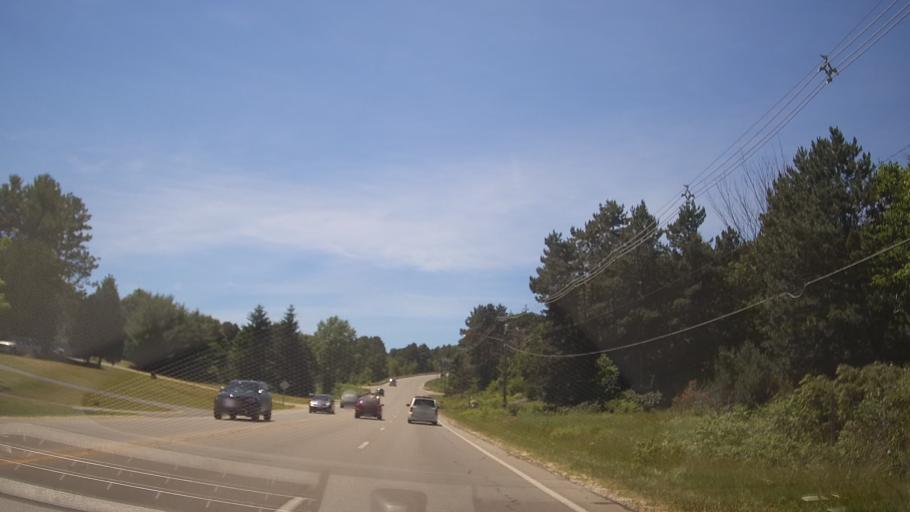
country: US
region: Michigan
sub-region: Grand Traverse County
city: Traverse City
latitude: 44.7275
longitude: -85.6670
